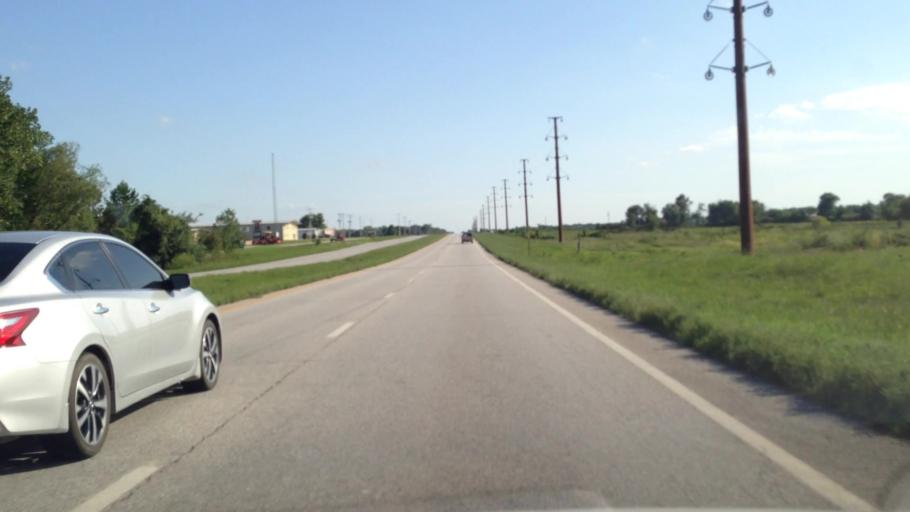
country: US
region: Kansas
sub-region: Crawford County
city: Frontenac
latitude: 37.4927
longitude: -94.7050
